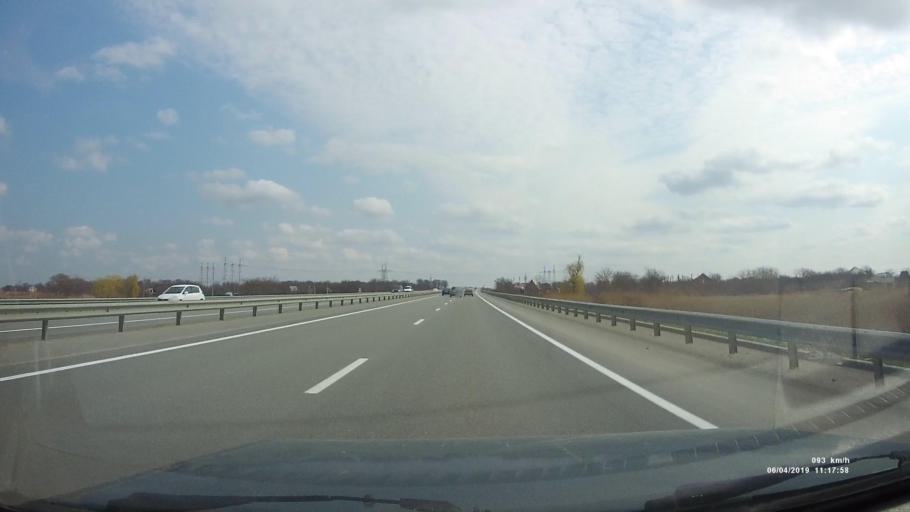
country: RU
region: Rostov
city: Kuleshovka
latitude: 47.0972
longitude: 39.5933
